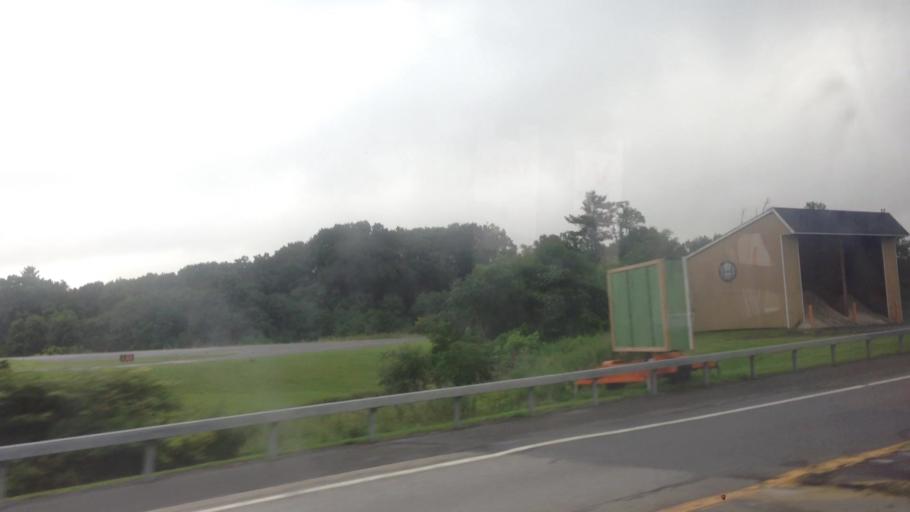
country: US
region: New York
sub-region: Ulster County
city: Lake Katrine
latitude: 41.9813
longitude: -73.9618
